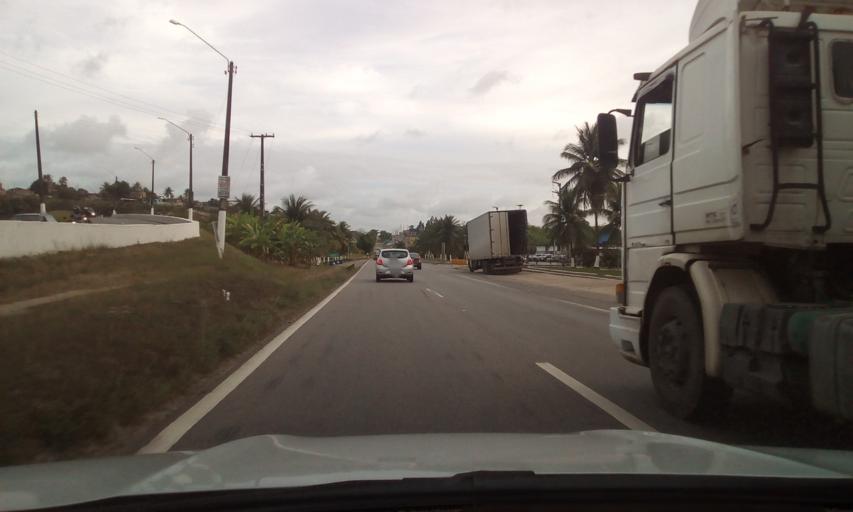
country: BR
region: Pernambuco
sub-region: Igarassu
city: Igarassu
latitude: -7.8324
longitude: -34.9137
